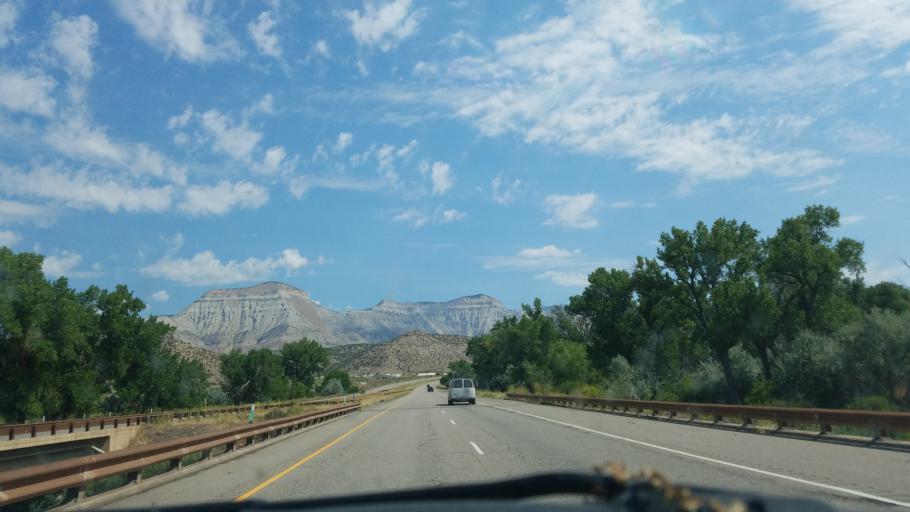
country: US
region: Colorado
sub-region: Garfield County
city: Parachute
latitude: 39.3388
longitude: -108.1930
